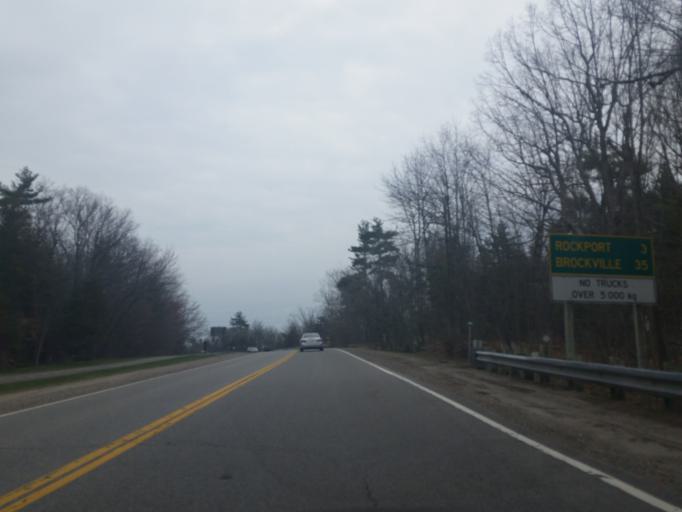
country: US
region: New York
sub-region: Jefferson County
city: Alexandria Bay
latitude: 44.3684
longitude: -75.9726
